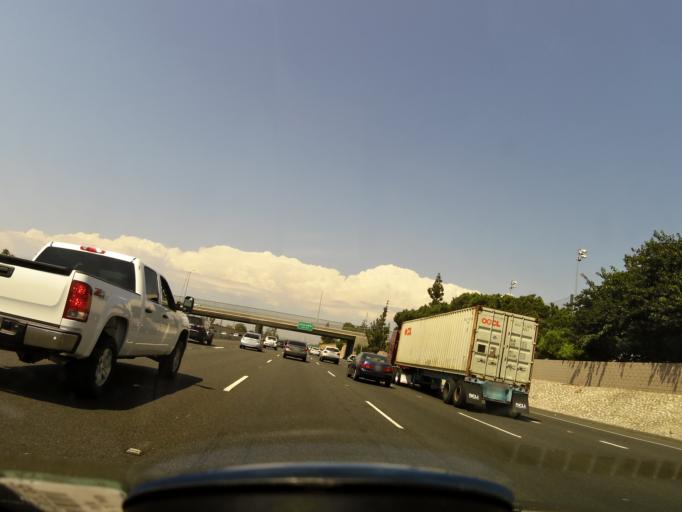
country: US
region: California
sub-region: Orange County
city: Villa Park
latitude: 33.8010
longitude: -117.8313
